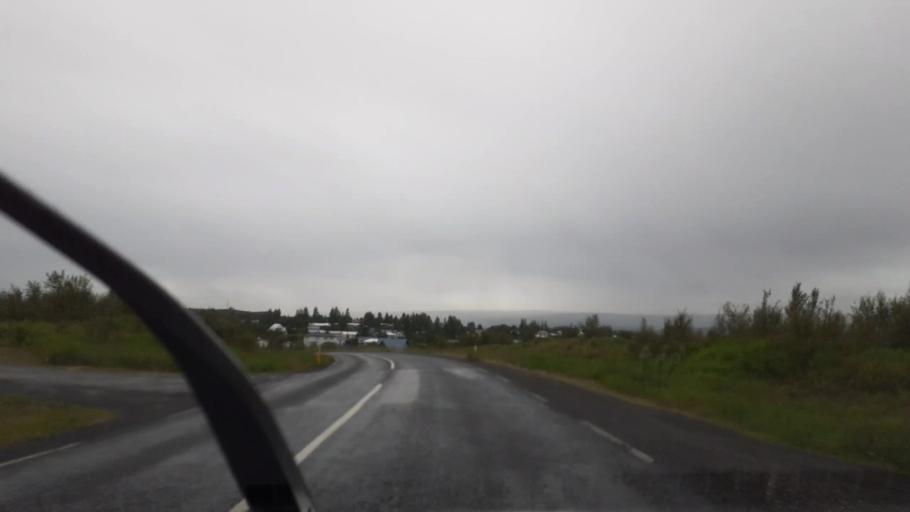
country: IS
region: East
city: Egilsstadir
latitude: 65.2679
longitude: -14.3769
